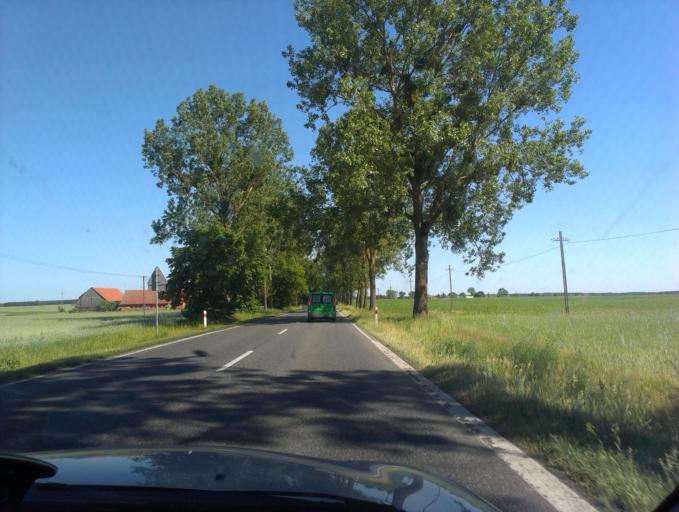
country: PL
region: Kujawsko-Pomorskie
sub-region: Powiat swiecki
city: Bukowiec
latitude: 53.4612
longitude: 18.1861
